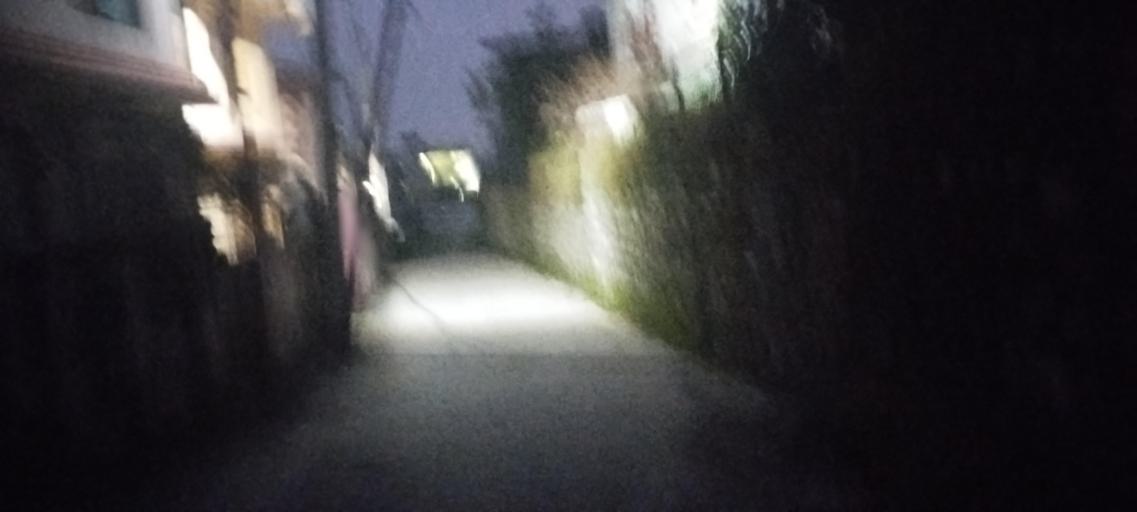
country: NP
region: Central Region
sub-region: Bagmati Zone
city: Kathmandu
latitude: 27.7731
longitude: 85.3632
